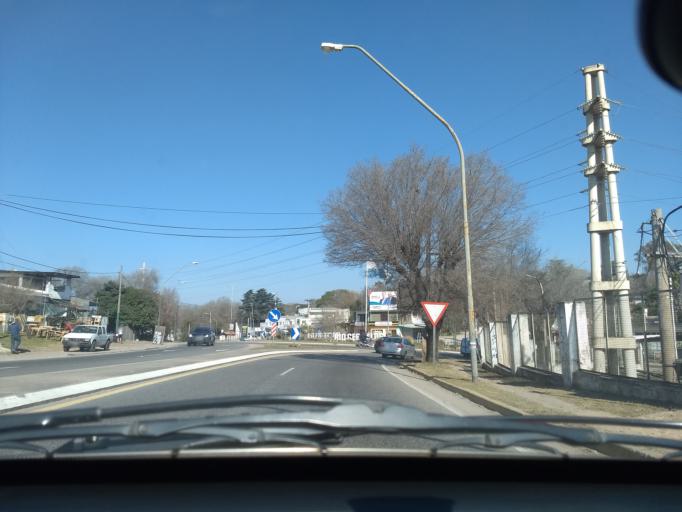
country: AR
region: Cordoba
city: Rio Ceballos
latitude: -31.1742
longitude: -64.3013
